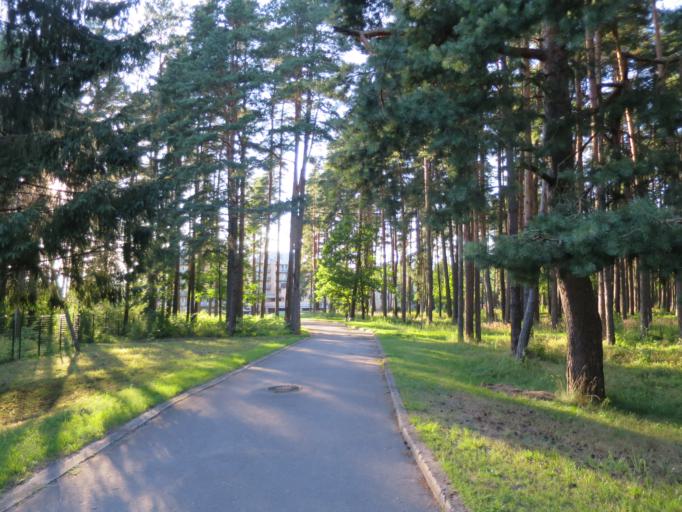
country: LV
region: Riga
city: Bergi
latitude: 56.9779
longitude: 24.3069
